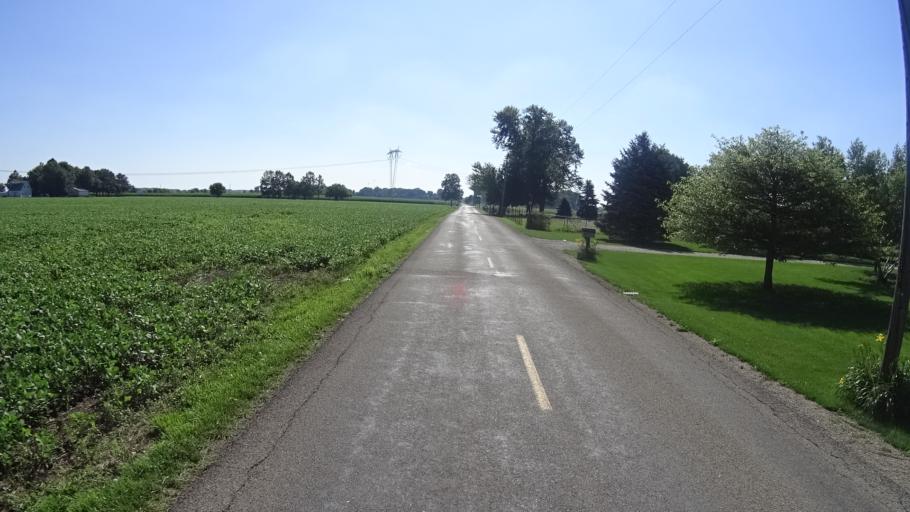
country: US
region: Indiana
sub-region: Madison County
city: Ingalls
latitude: 39.9878
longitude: -85.8186
